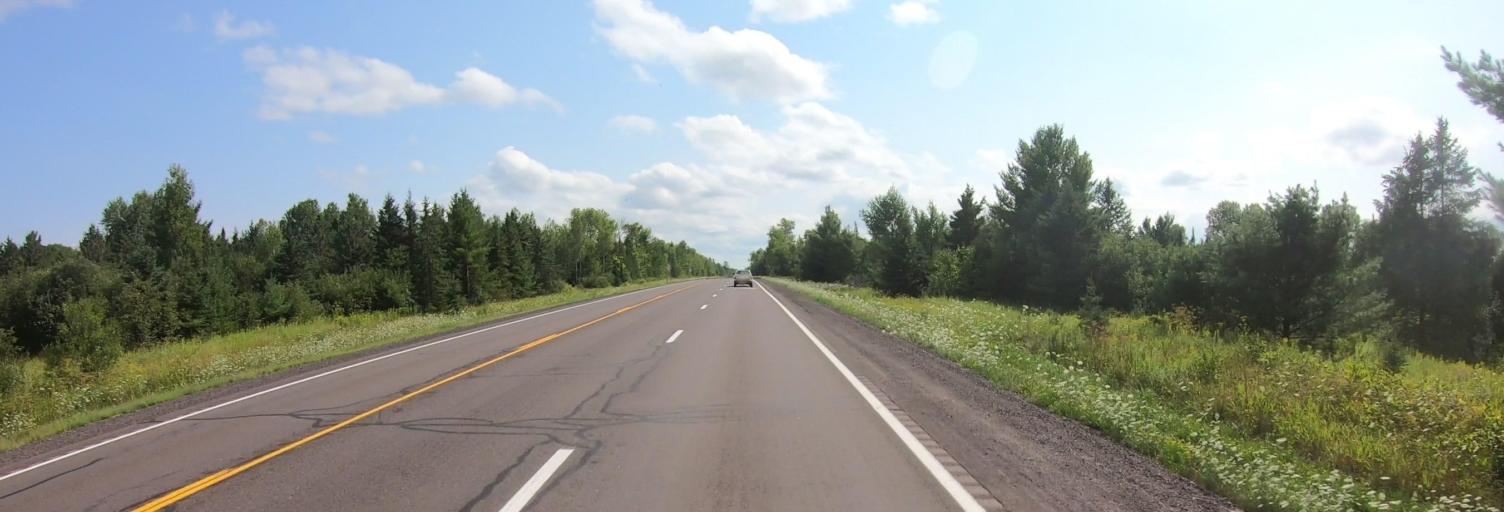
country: US
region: Michigan
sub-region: Ontonagon County
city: Ontonagon
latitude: 46.6705
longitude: -89.1689
